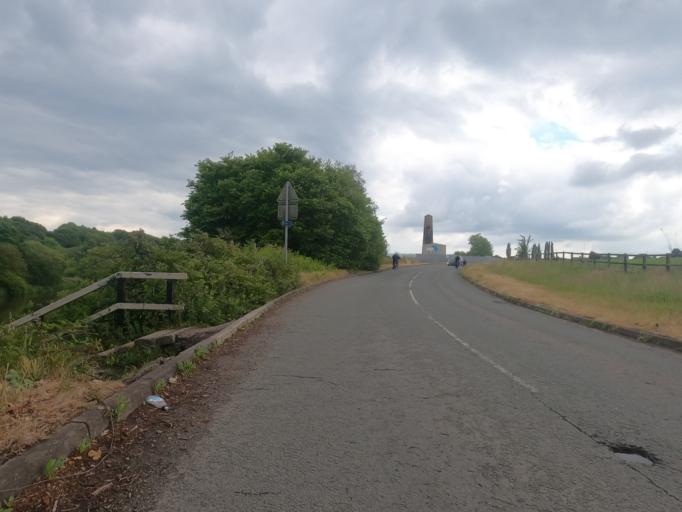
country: GB
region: England
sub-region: Cheshire West and Chester
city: Winsford
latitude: 53.2142
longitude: -2.5240
